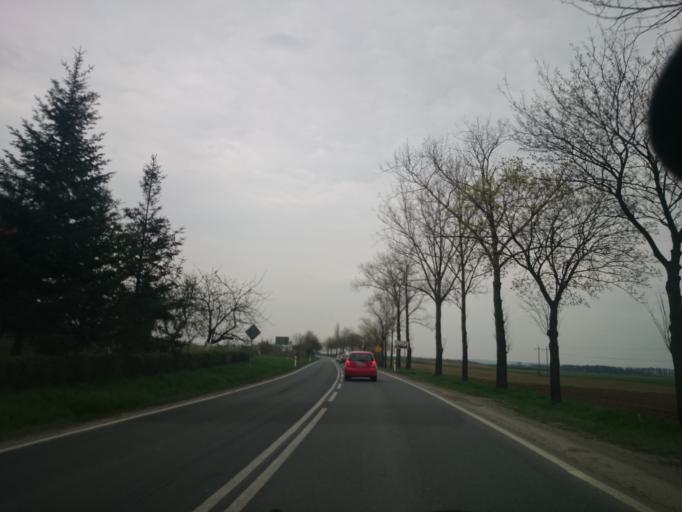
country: PL
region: Opole Voivodeship
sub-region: Powiat nyski
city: Otmuchow
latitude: 50.4679
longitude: 17.2212
